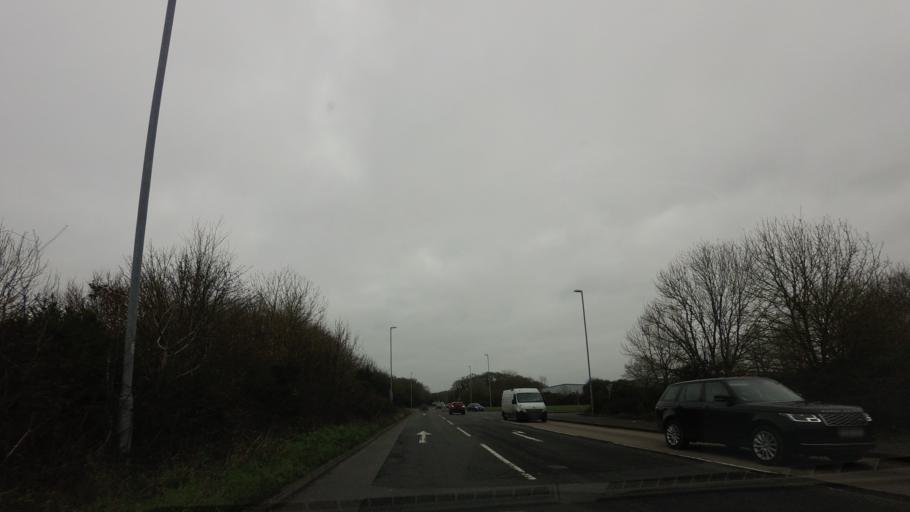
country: GB
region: England
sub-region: East Sussex
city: Saint Leonards-on-Sea
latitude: 50.8807
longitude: 0.5326
